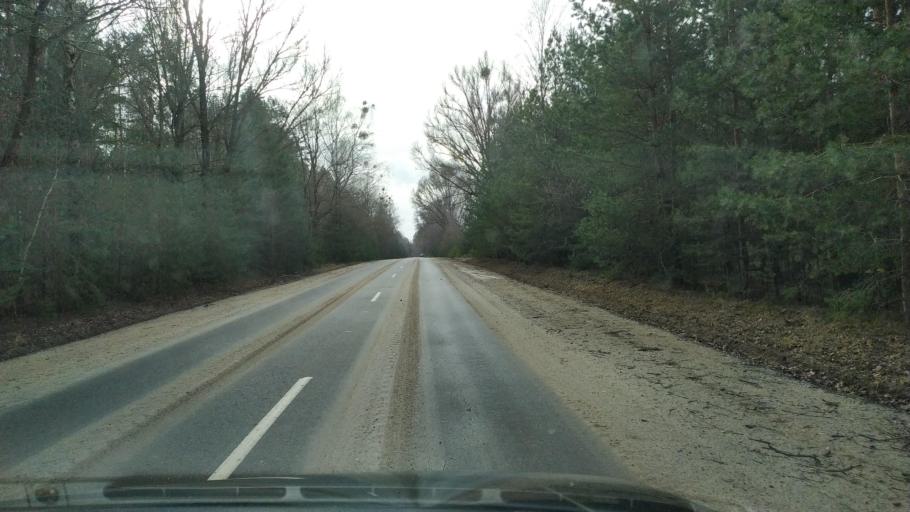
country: BY
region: Brest
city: Kamyanyets
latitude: 52.4048
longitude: 23.9069
